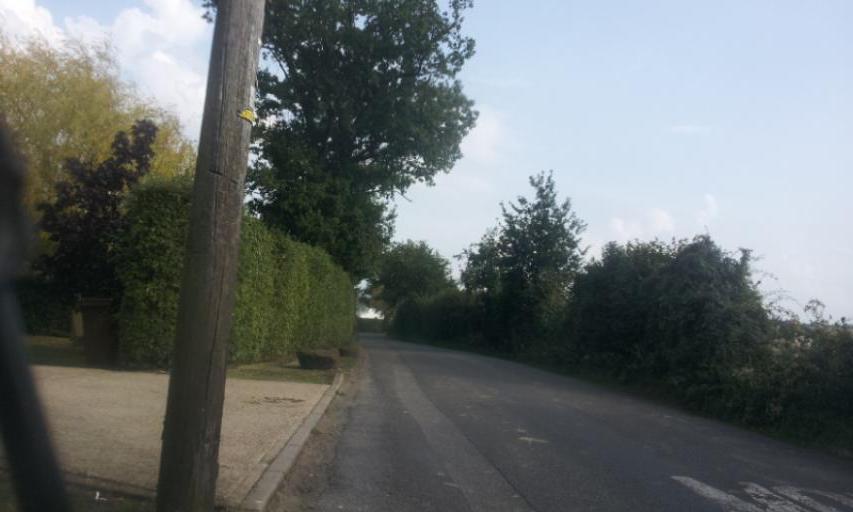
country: GB
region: England
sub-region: Kent
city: Paddock Wood
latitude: 51.1686
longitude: 0.4012
